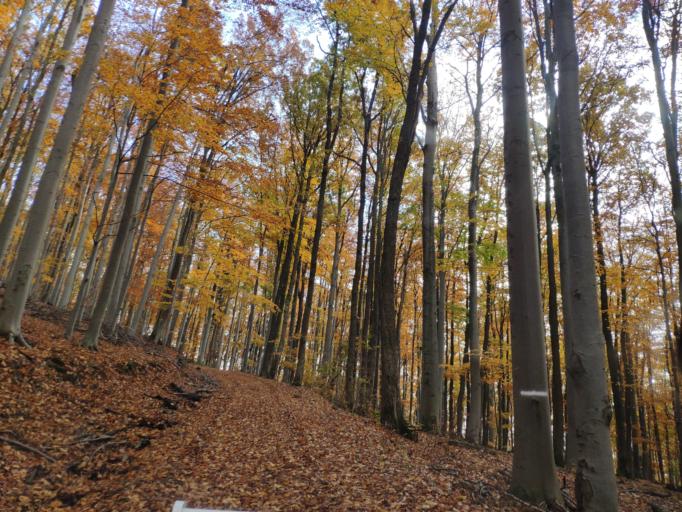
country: SK
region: Kosicky
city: Medzev
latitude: 48.7326
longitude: 20.9940
